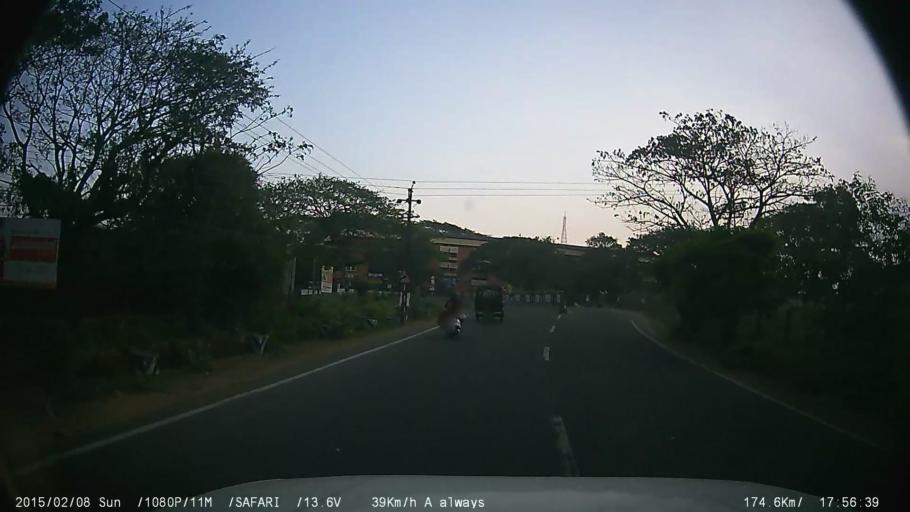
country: IN
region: Kerala
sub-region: Palakkad district
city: Palakkad
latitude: 10.7633
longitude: 76.6586
